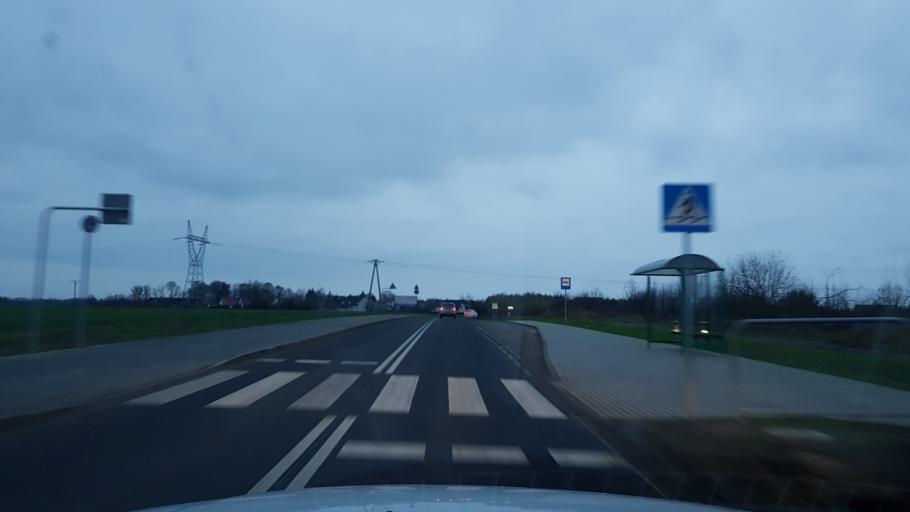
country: PL
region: West Pomeranian Voivodeship
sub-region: Powiat policki
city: Przeclaw
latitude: 53.4152
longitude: 14.4626
